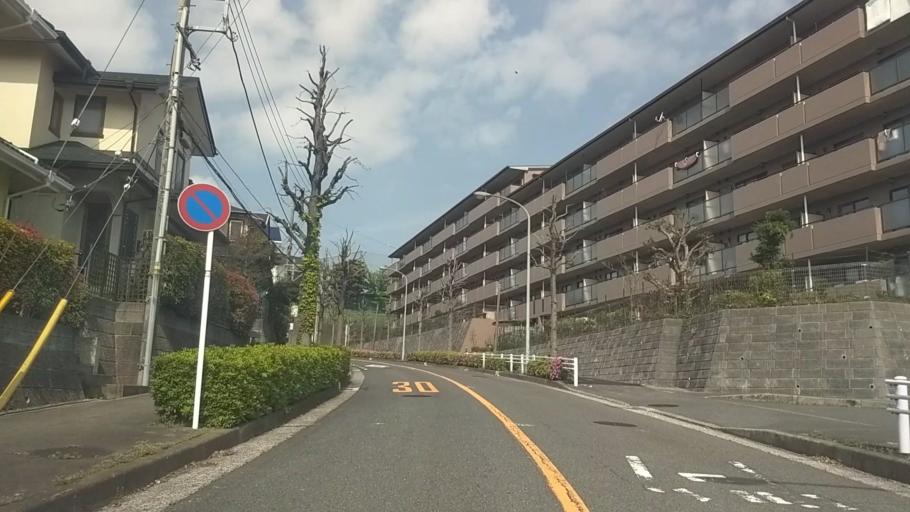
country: JP
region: Kanagawa
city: Yokohama
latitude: 35.3716
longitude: 139.6224
